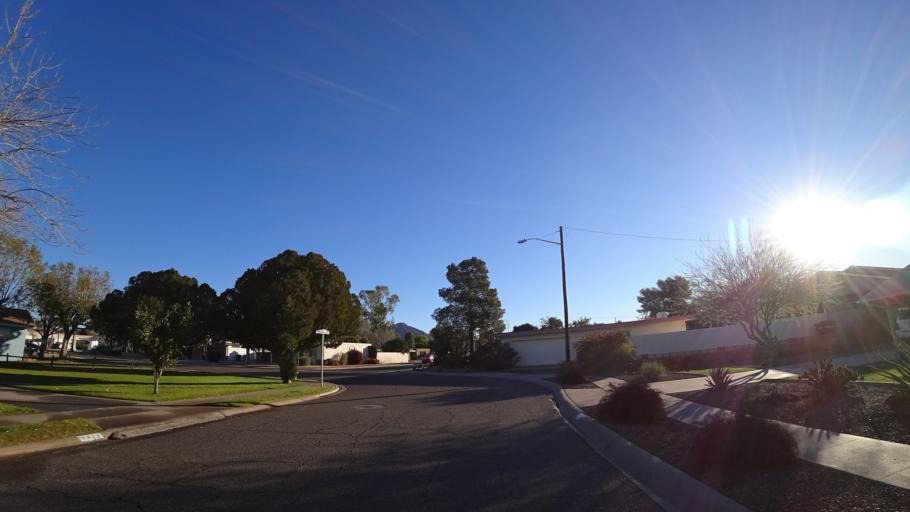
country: US
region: Arizona
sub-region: Maricopa County
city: Paradise Valley
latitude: 33.4923
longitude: -112.0078
